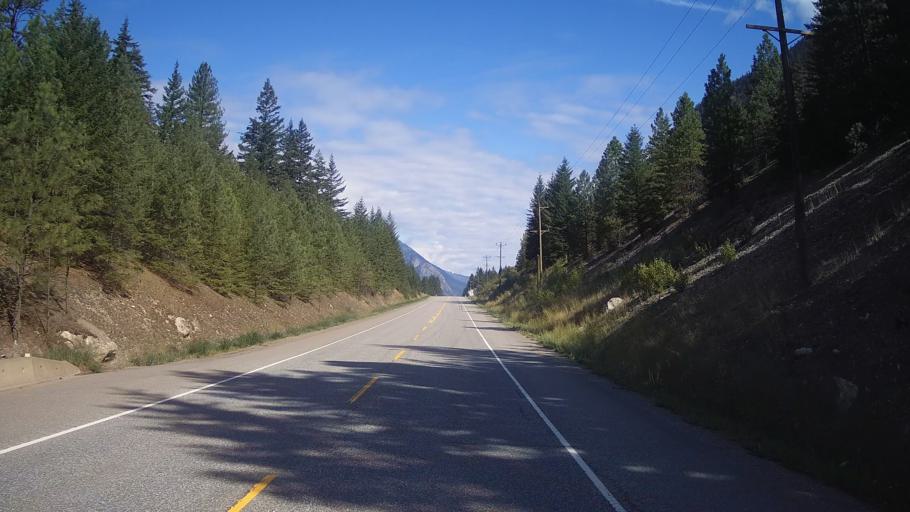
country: CA
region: British Columbia
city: Hope
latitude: 50.0324
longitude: -121.5310
